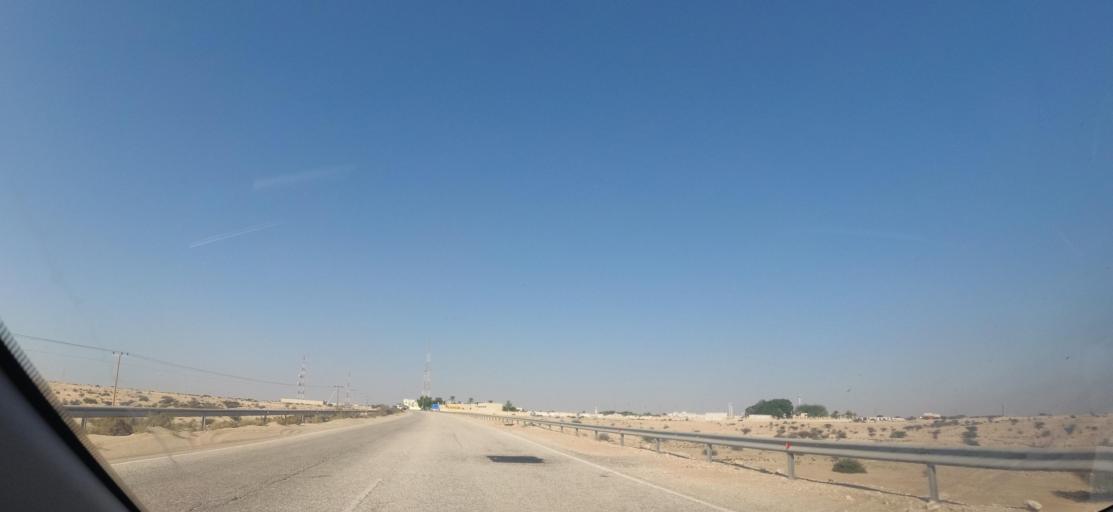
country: QA
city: Al Jumayliyah
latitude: 25.6136
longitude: 51.0787
